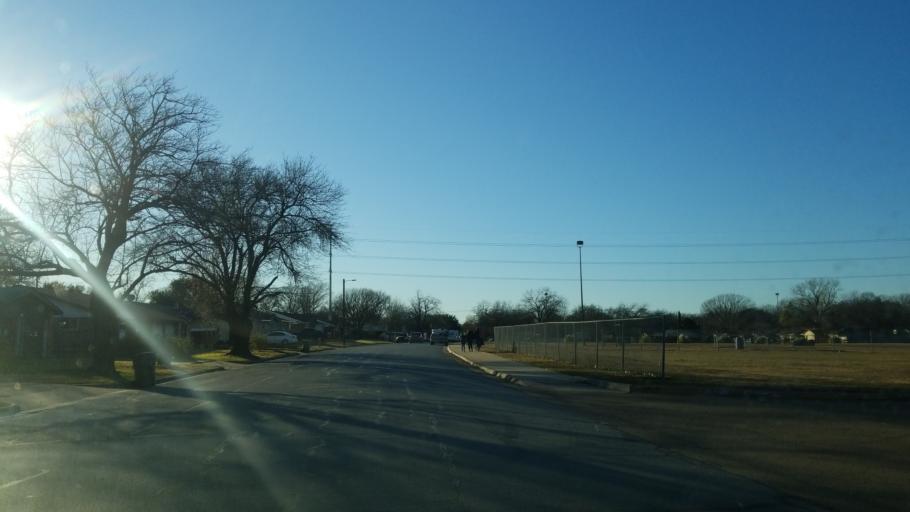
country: US
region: Texas
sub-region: Tarrant County
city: Arlington
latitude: 32.7258
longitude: -97.0695
